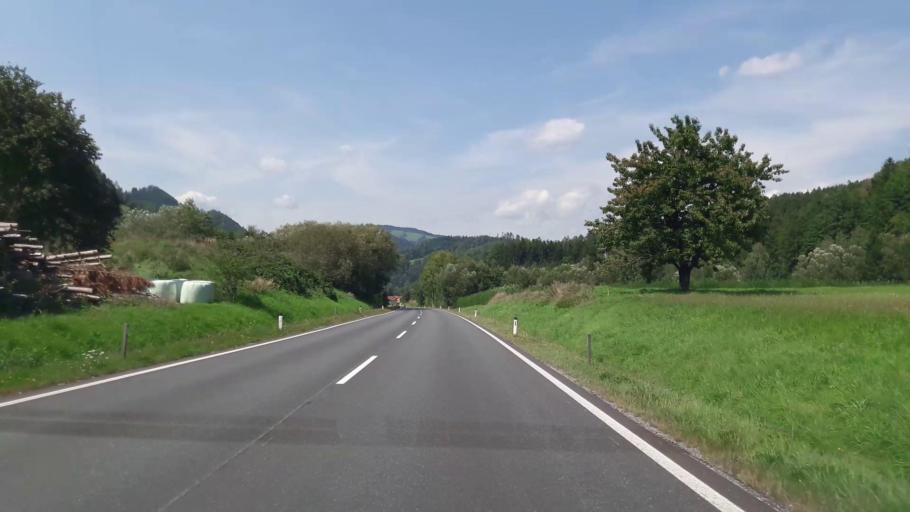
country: AT
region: Styria
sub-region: Politischer Bezirk Weiz
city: Anger
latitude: 47.2824
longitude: 15.6914
